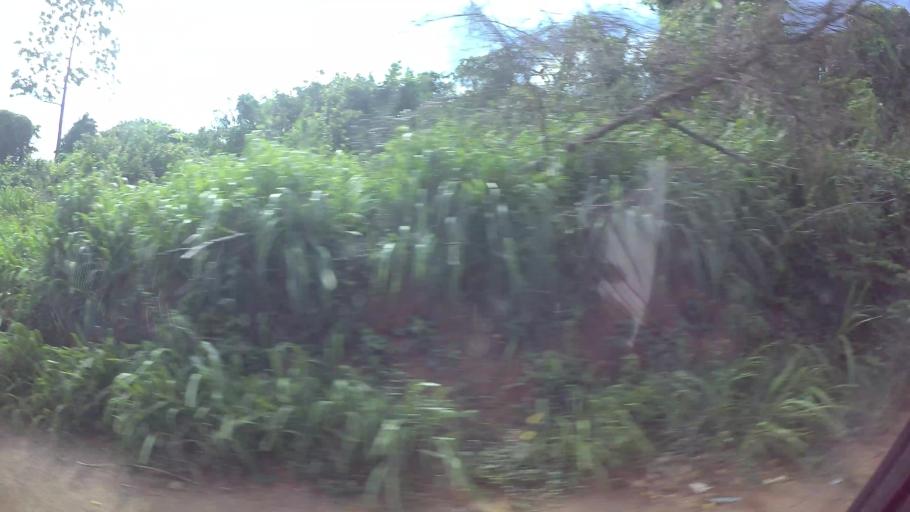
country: TH
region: Chon Buri
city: Sattahip
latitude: 12.6886
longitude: 100.9128
